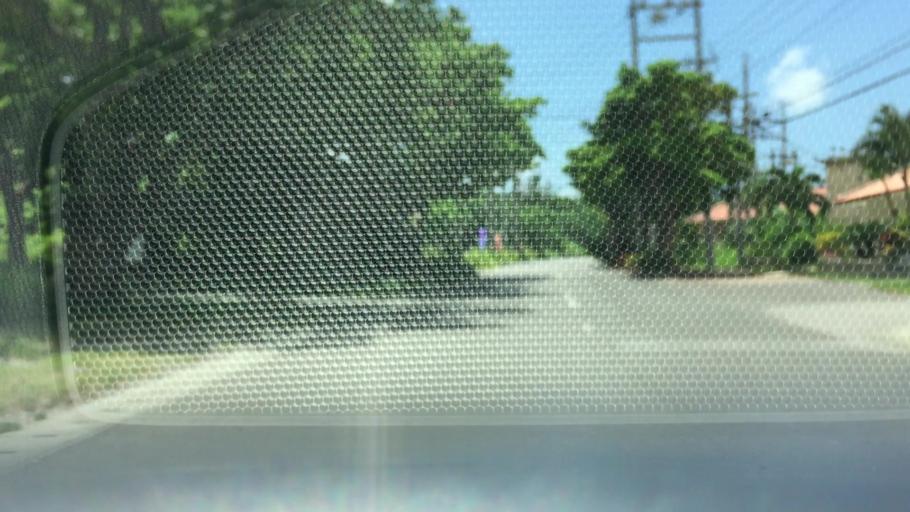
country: JP
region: Okinawa
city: Ishigaki
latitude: 24.3640
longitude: 124.1156
